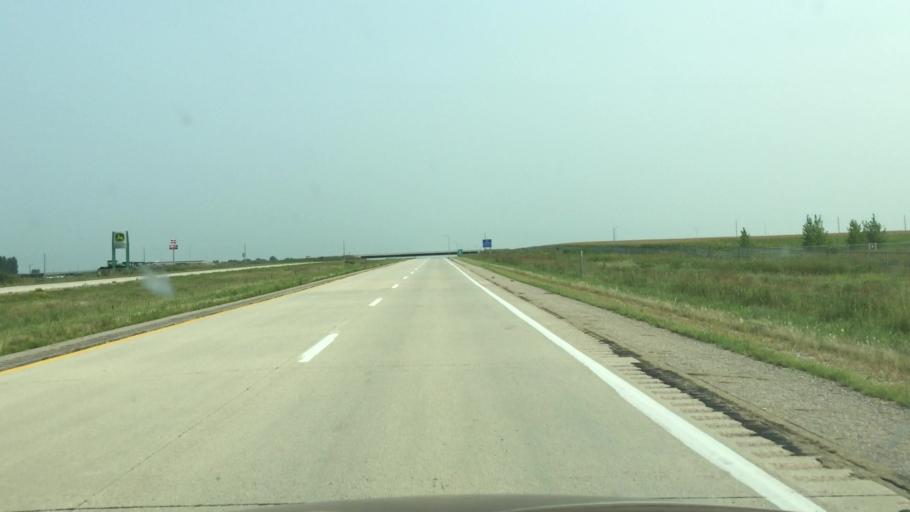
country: US
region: Iowa
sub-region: Osceola County
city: Sibley
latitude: 43.3982
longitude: -95.7171
